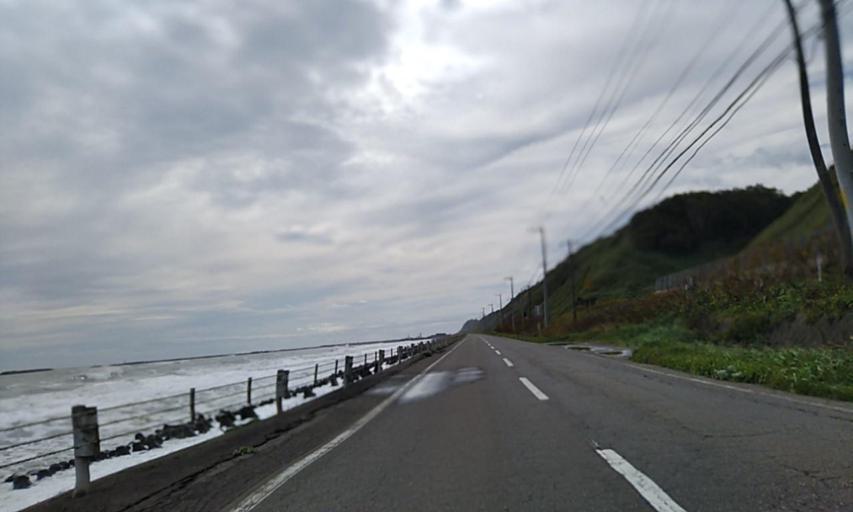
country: JP
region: Hokkaido
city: Kushiro
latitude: 42.8139
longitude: 143.8292
